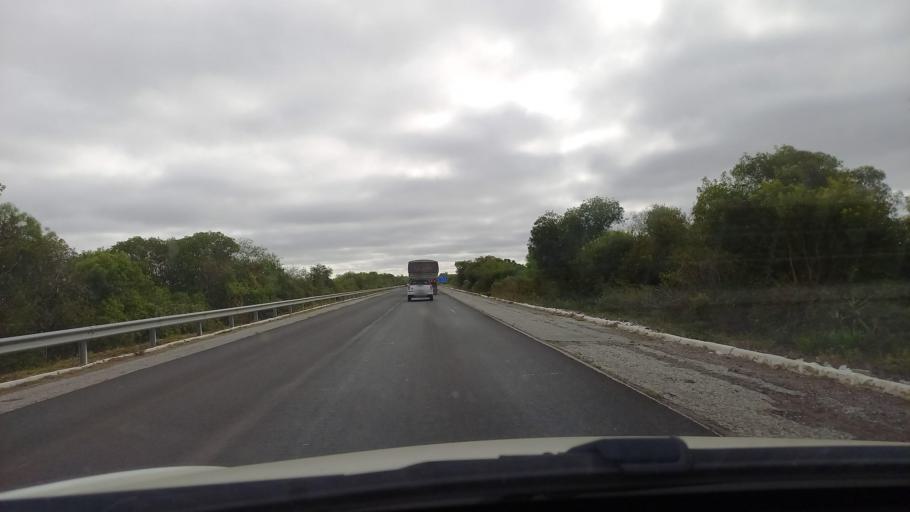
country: BR
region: Rio Grande do Sul
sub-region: Dom Pedrito
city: Dom Pedrito
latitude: -30.9495
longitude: -54.7084
